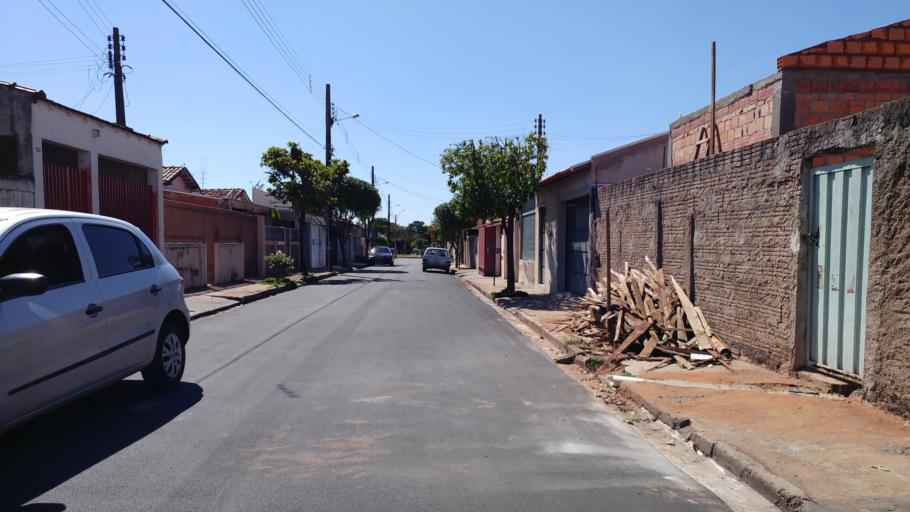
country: BR
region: Sao Paulo
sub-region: Paraguacu Paulista
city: Paraguacu Paulista
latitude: -22.4296
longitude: -50.5820
